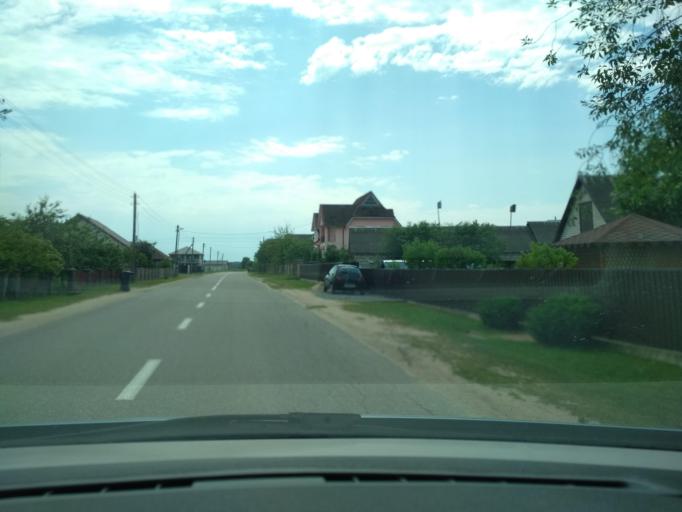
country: BY
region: Grodnenskaya
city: Astravyets
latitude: 54.6051
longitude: 25.9598
